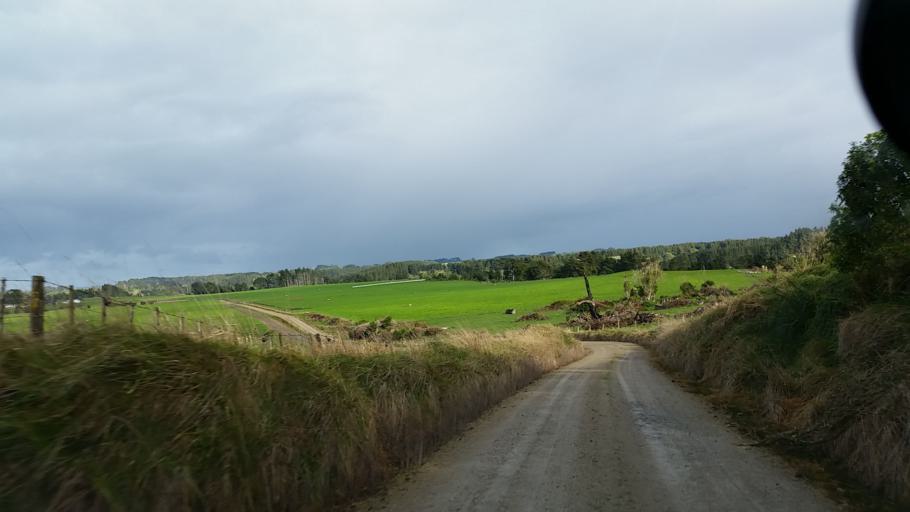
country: NZ
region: Taranaki
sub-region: South Taranaki District
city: Patea
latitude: -39.7299
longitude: 174.7084
